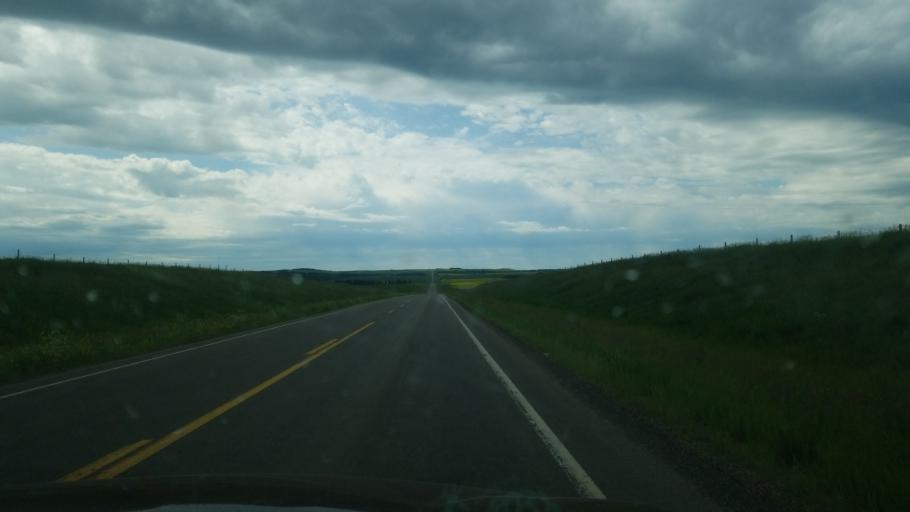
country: CA
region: Saskatchewan
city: Unity
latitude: 52.9154
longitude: -109.3425
